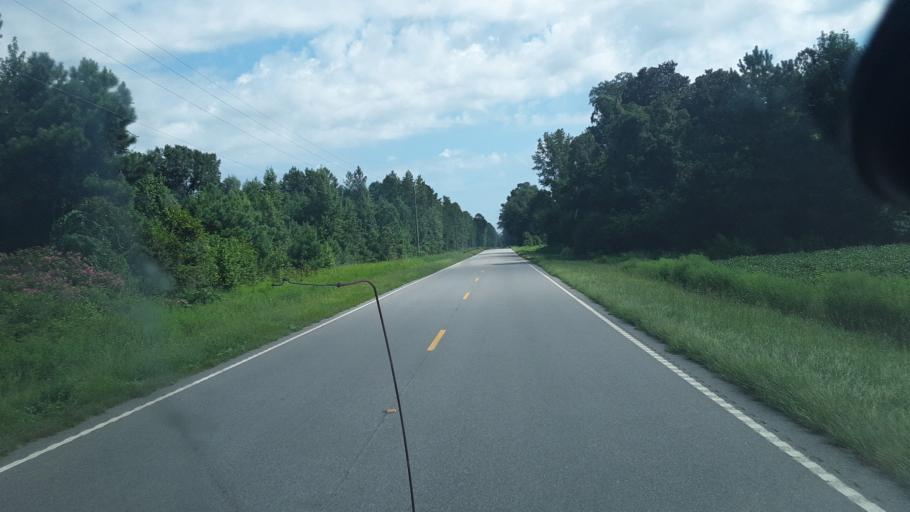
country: US
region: South Carolina
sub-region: Bamberg County
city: Bamberg
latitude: 33.0785
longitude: -81.0234
